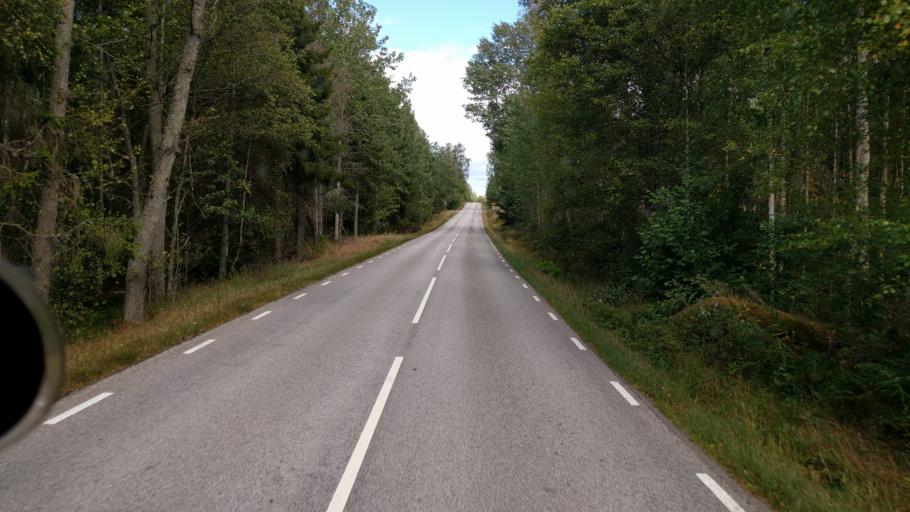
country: SE
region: Kalmar
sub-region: Vasterviks Kommun
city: Ankarsrum
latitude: 57.7845
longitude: 16.1692
